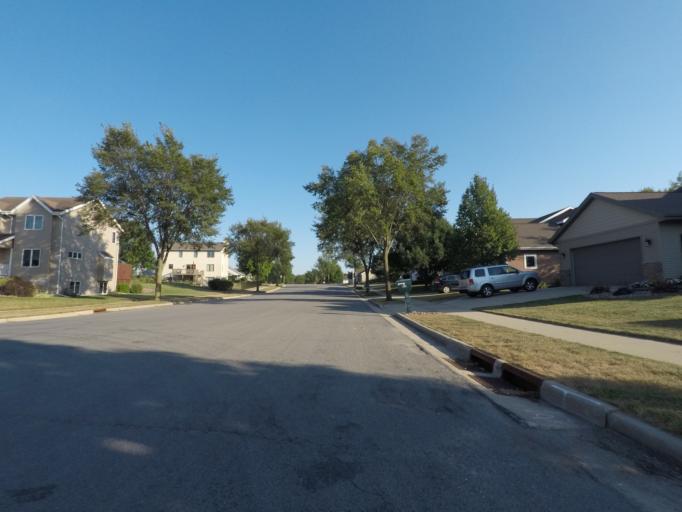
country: US
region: Wisconsin
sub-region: Dane County
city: Verona
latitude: 43.0049
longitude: -89.5419
